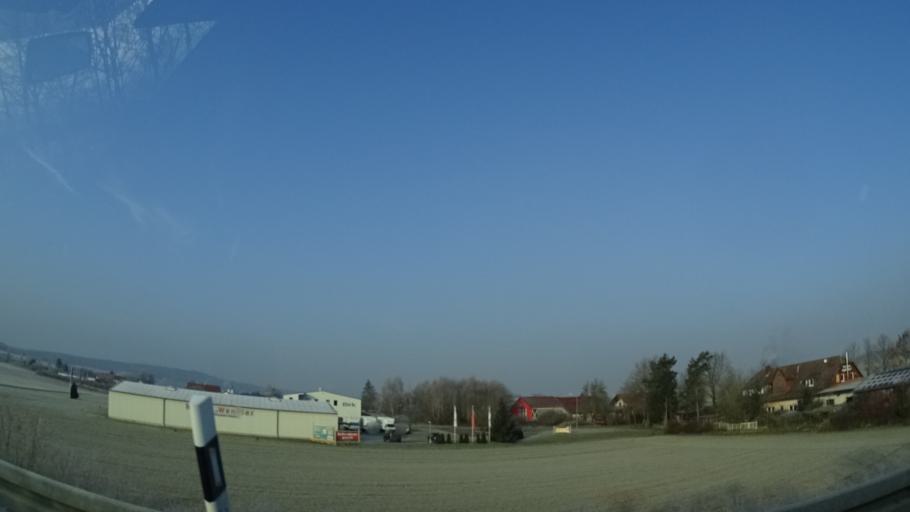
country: DE
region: Bavaria
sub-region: Upper Franconia
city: Sesslach
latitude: 50.2172
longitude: 10.8323
